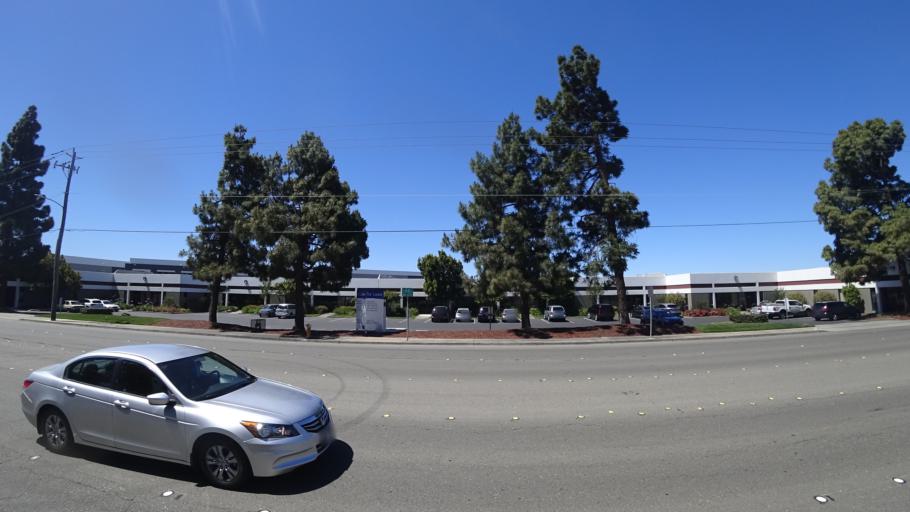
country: US
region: California
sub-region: Alameda County
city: Hayward
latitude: 37.6185
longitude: -122.0959
